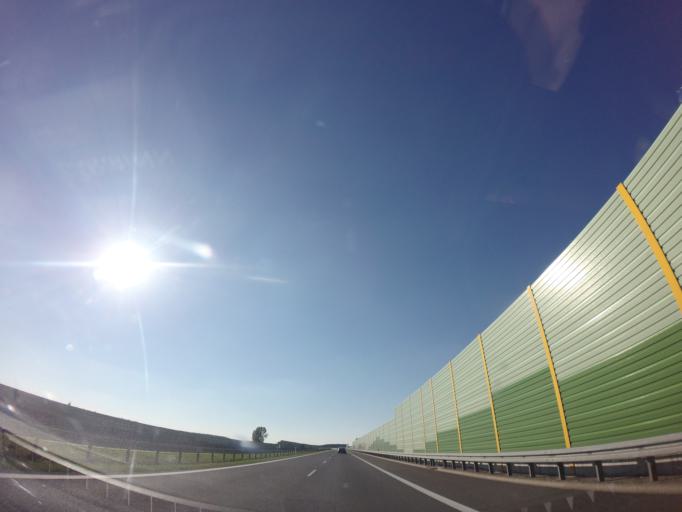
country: PL
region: Lubusz
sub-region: Powiat gorzowski
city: Deszczno
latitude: 52.6866
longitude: 15.2843
